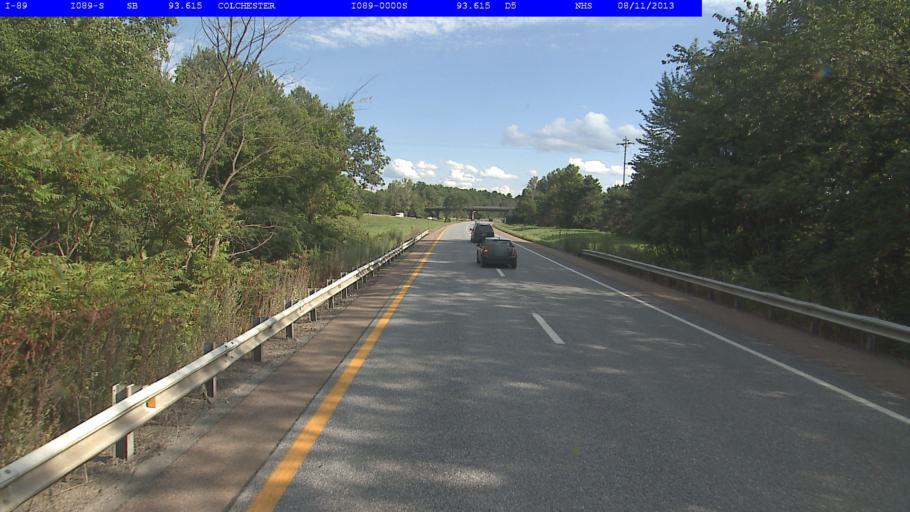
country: US
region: Vermont
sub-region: Chittenden County
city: Winooski
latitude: 44.5329
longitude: -73.1970
